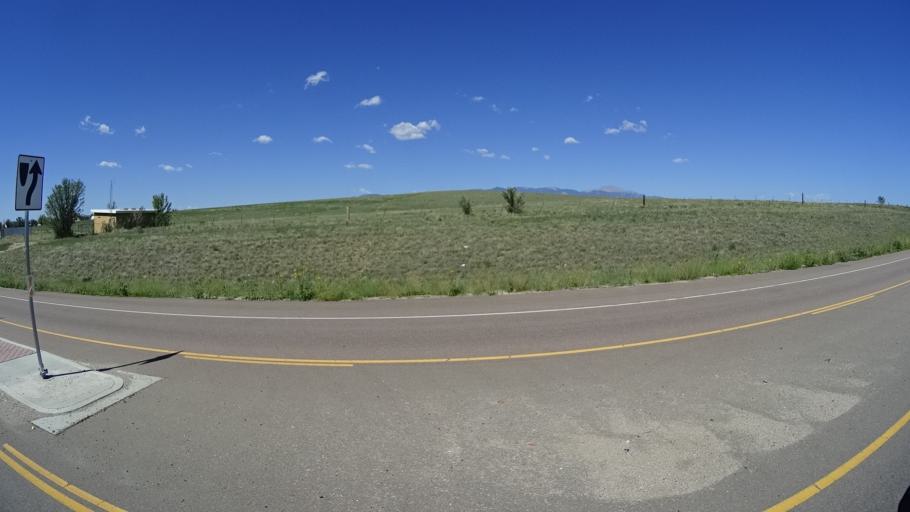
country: US
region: Colorado
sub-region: El Paso County
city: Security-Widefield
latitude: 38.7454
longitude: -104.6479
